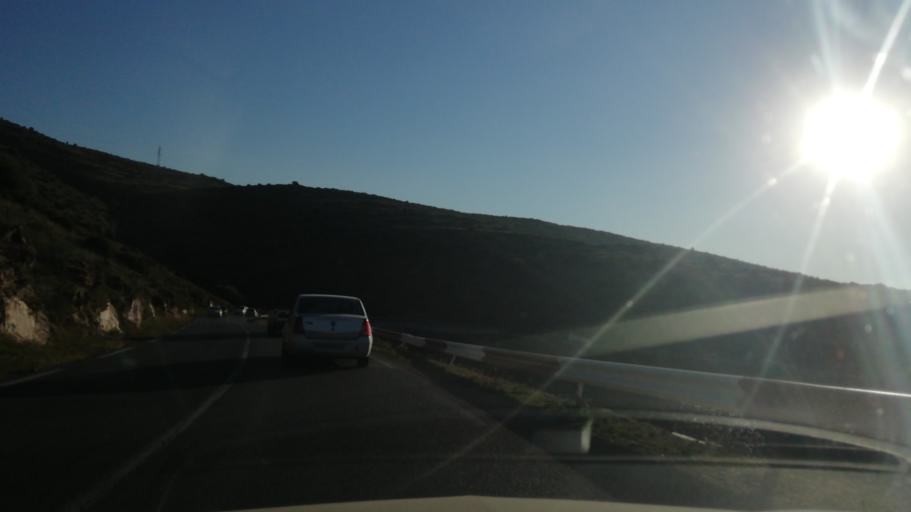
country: DZ
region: Tlemcen
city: Beni Mester
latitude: 34.8493
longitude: -1.4595
